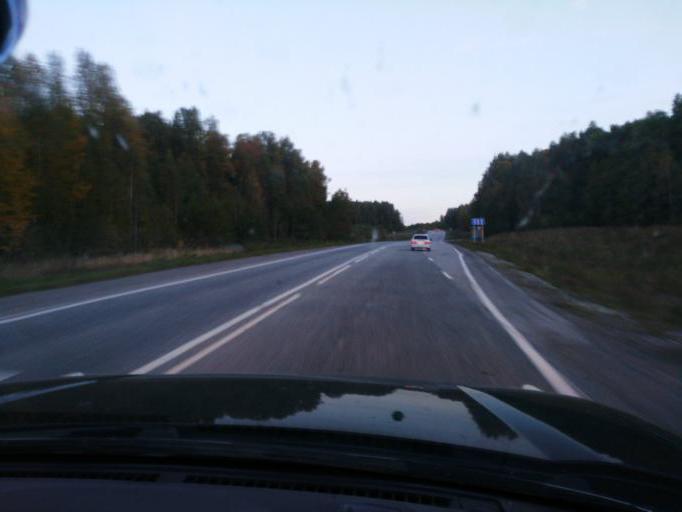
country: RU
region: Perm
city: Verkhnechusovskiye Gorodki
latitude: 58.2899
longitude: 56.8970
